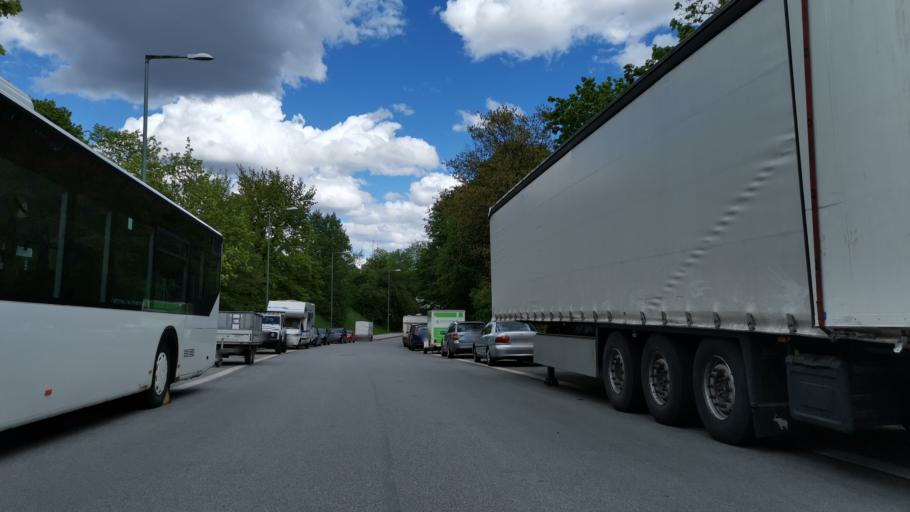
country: DE
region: Bavaria
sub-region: Upper Bavaria
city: Munich
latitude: 48.1279
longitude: 11.5221
